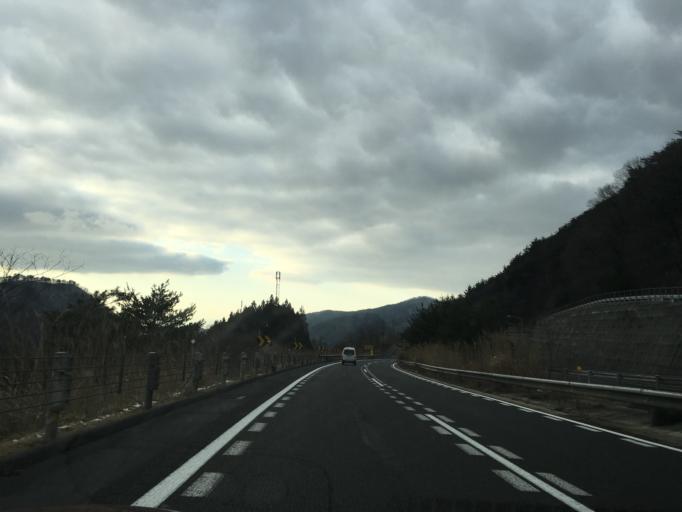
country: JP
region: Yamagata
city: Yamagata-shi
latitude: 38.2284
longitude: 140.4109
